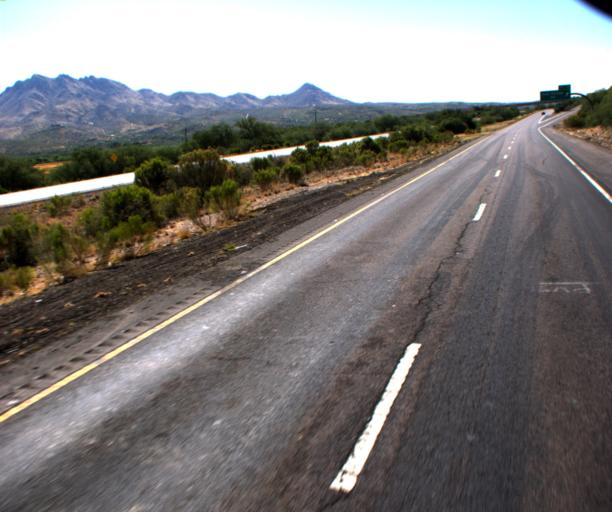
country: US
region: Arizona
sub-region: Santa Cruz County
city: Rio Rico
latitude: 31.5314
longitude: -111.0291
